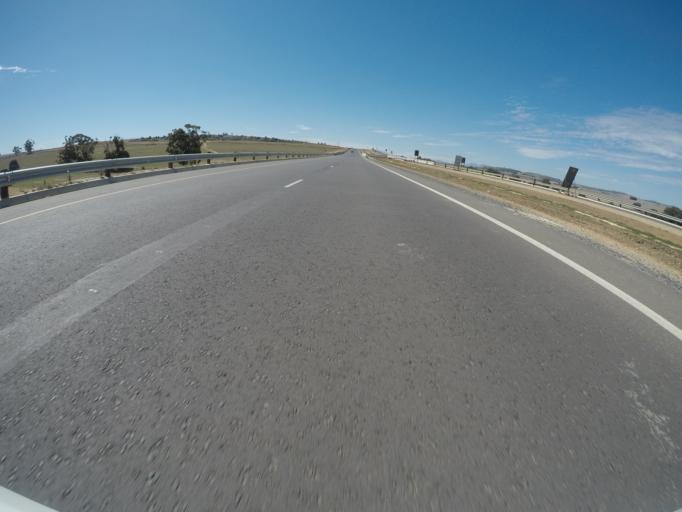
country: ZA
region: Western Cape
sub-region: West Coast District Municipality
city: Malmesbury
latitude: -33.4776
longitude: 18.6866
